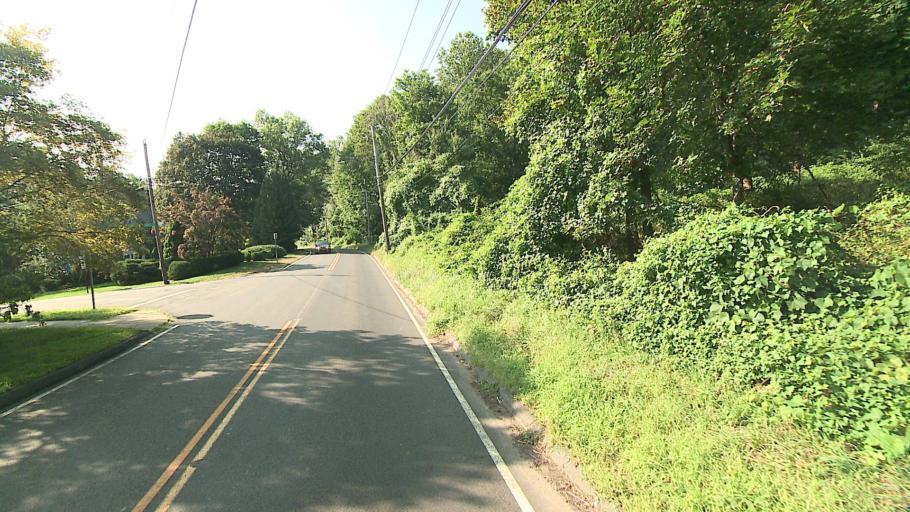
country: US
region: Connecticut
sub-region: New Haven County
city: New Haven
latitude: 41.3149
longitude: -72.9709
